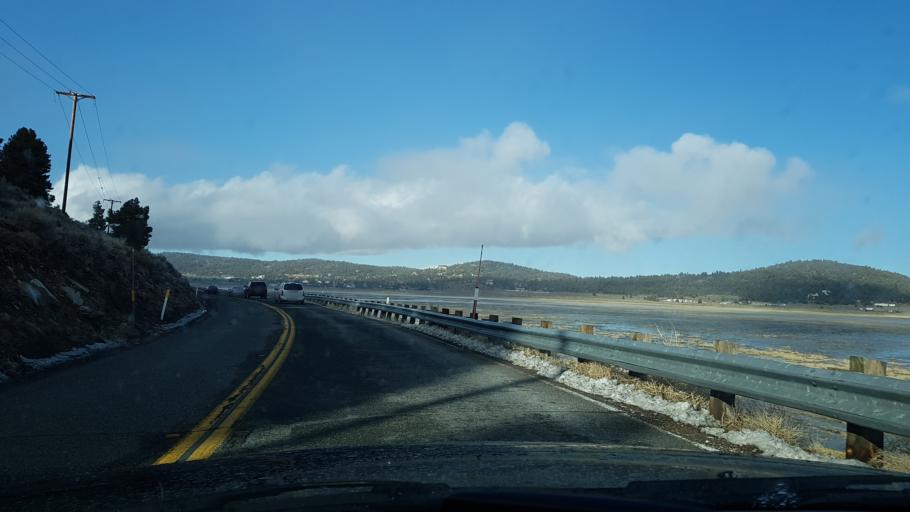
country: US
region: California
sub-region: San Bernardino County
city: Big Bear City
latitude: 34.2767
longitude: -116.8142
